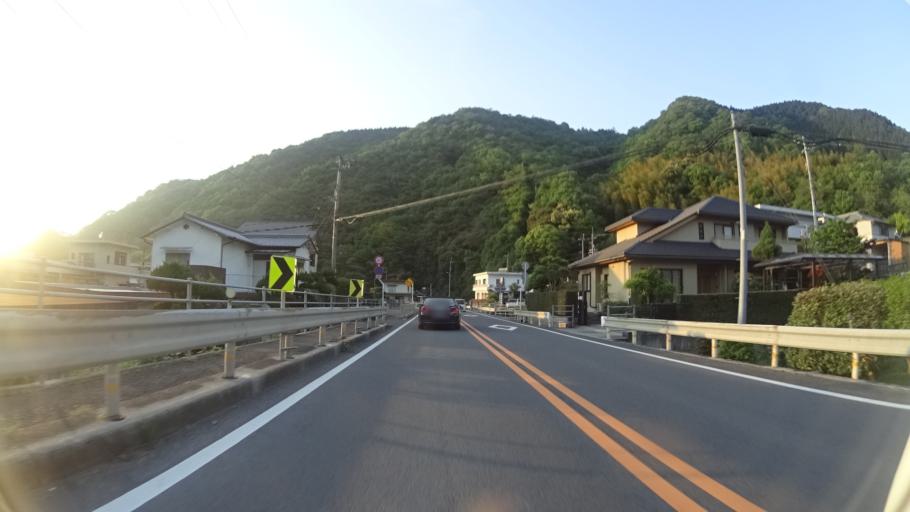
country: JP
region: Ehime
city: Kawanoecho
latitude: 33.9908
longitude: 133.6272
